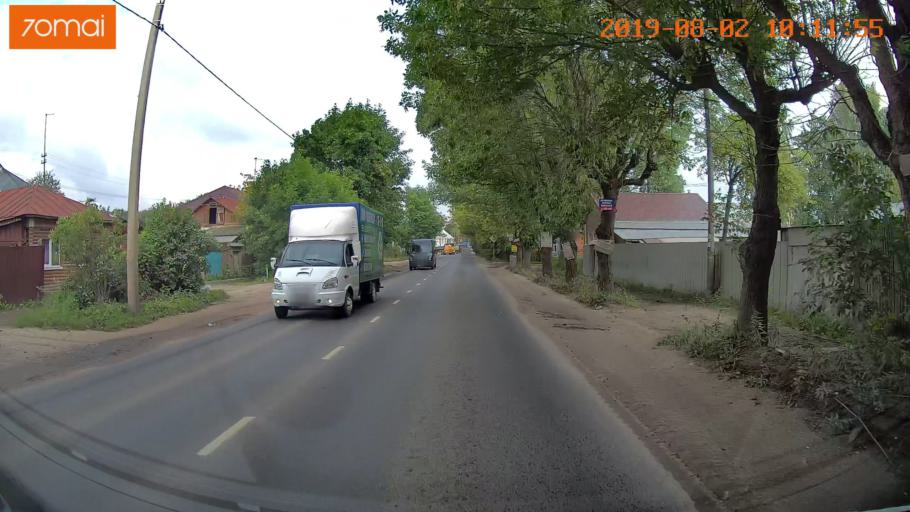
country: RU
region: Ivanovo
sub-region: Gorod Ivanovo
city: Ivanovo
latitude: 56.9961
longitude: 40.9512
